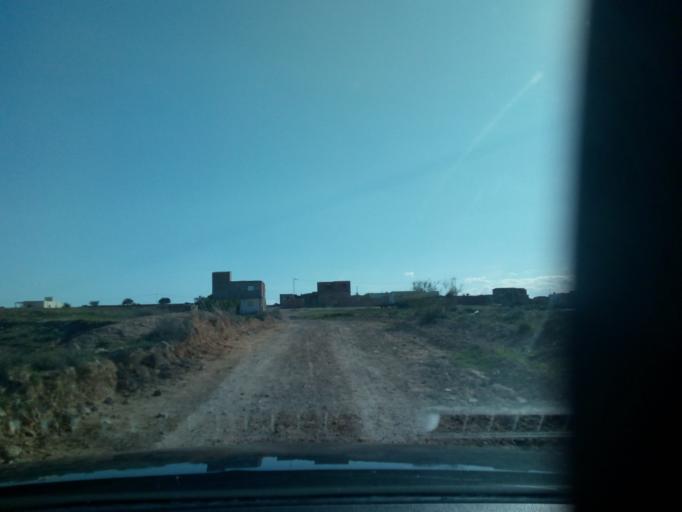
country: TN
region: Safaqis
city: Sfax
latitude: 34.7228
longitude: 10.6120
